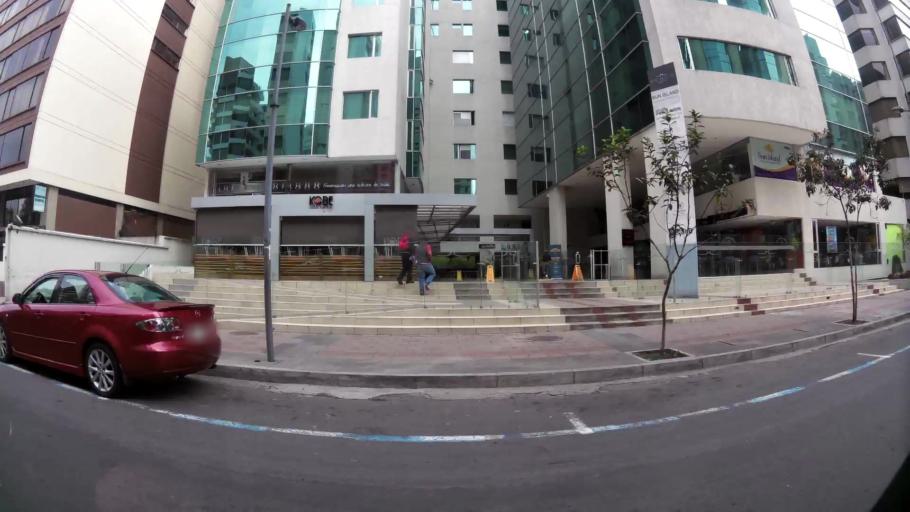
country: EC
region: Pichincha
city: Quito
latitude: -0.1811
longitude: -78.4802
